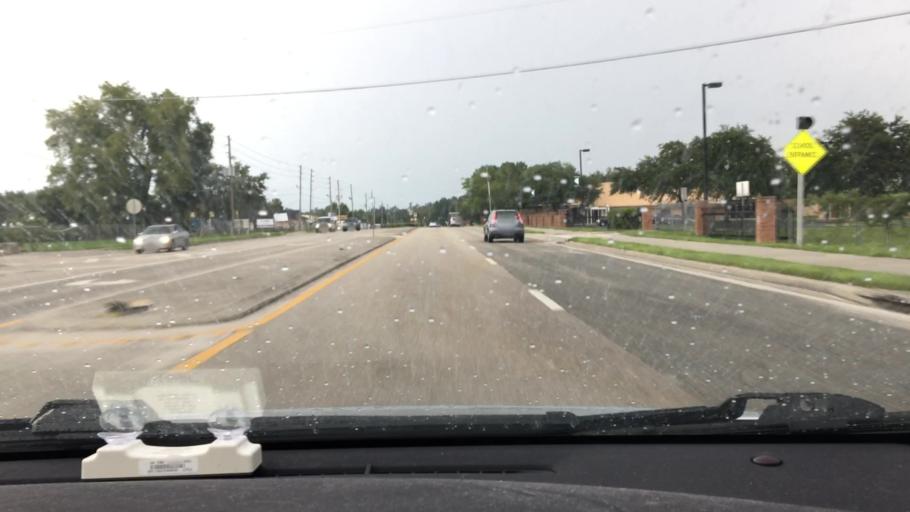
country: US
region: Florida
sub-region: Seminole County
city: Casselberry
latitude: 28.6787
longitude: -81.3485
